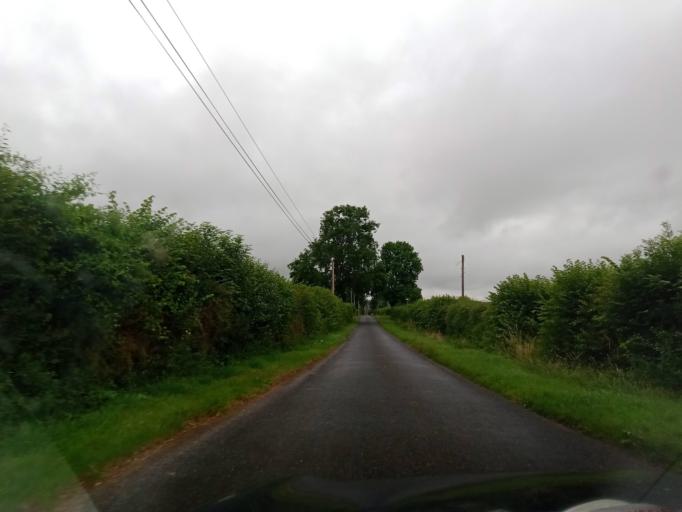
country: IE
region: Leinster
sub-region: Laois
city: Stradbally
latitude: 52.9573
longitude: -7.2117
